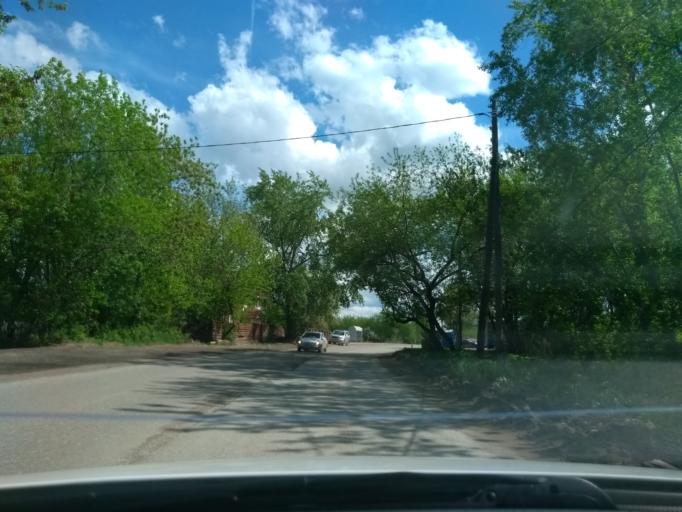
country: RU
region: Perm
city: Kondratovo
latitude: 58.0064
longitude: 56.1167
